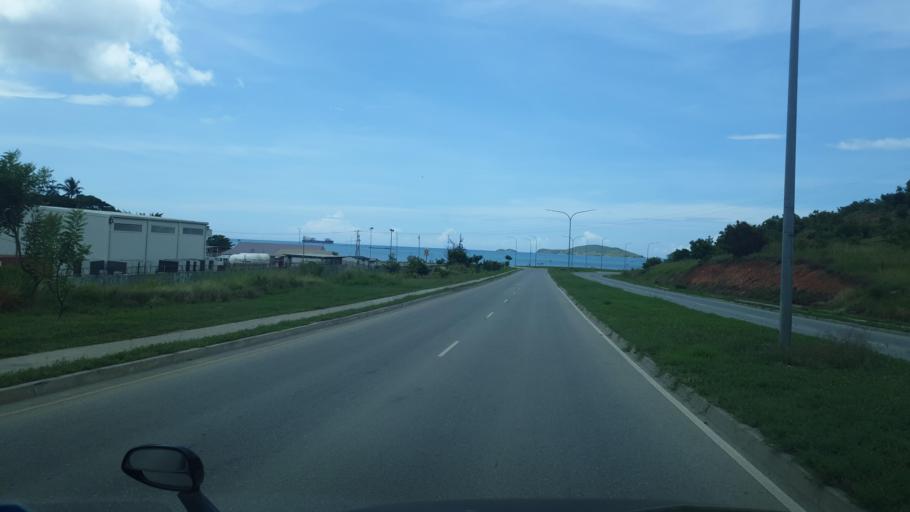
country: PG
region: National Capital
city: Port Moresby
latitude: -9.4360
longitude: 147.1392
